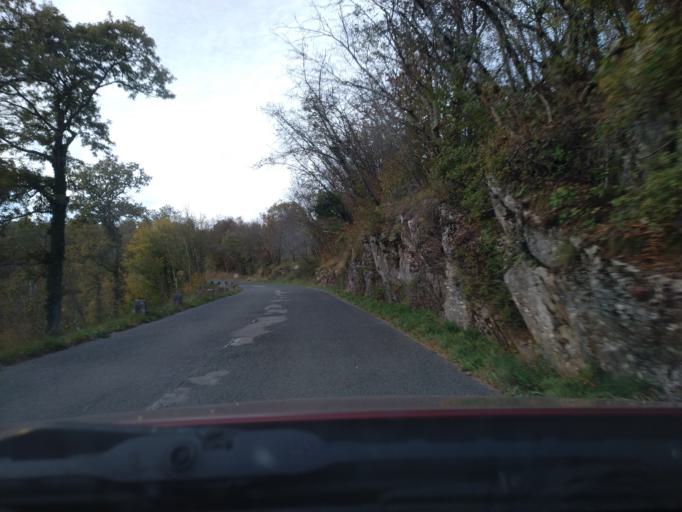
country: SI
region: Divaca
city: Divaca
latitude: 45.6629
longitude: 13.9857
